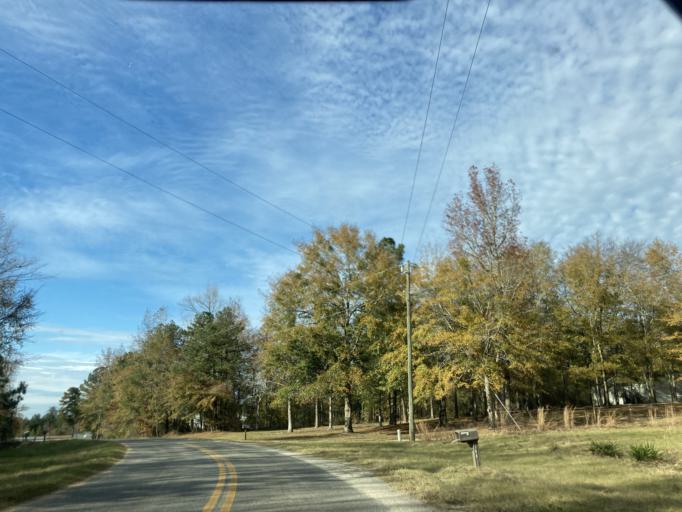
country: US
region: Georgia
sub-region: Jones County
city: Gray
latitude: 32.9141
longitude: -83.5142
